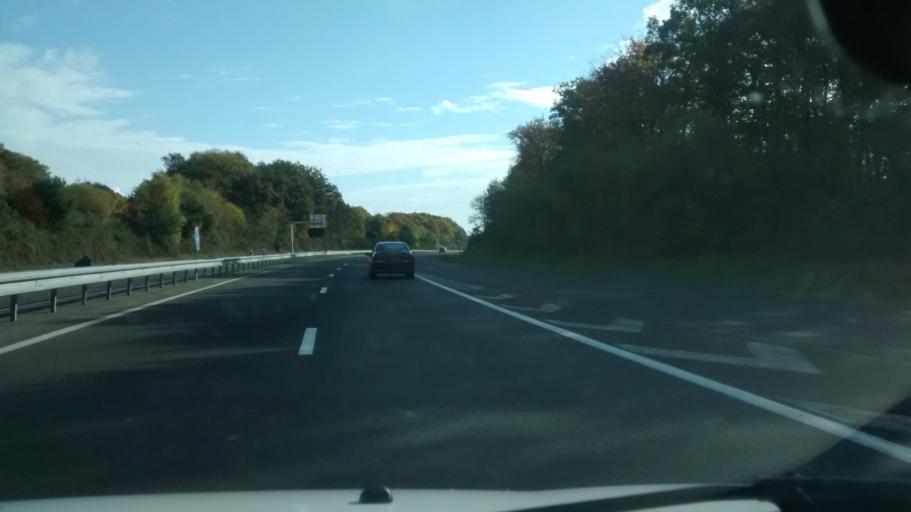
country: FR
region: Pays de la Loire
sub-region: Departement de Maine-et-Loire
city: Combree
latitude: 47.7147
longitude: -1.0099
